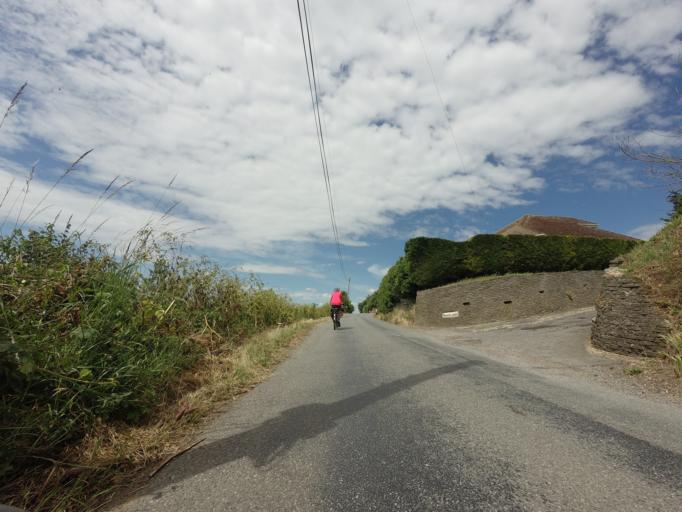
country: GB
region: England
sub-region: Kent
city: Strood
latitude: 51.4282
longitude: 0.4695
